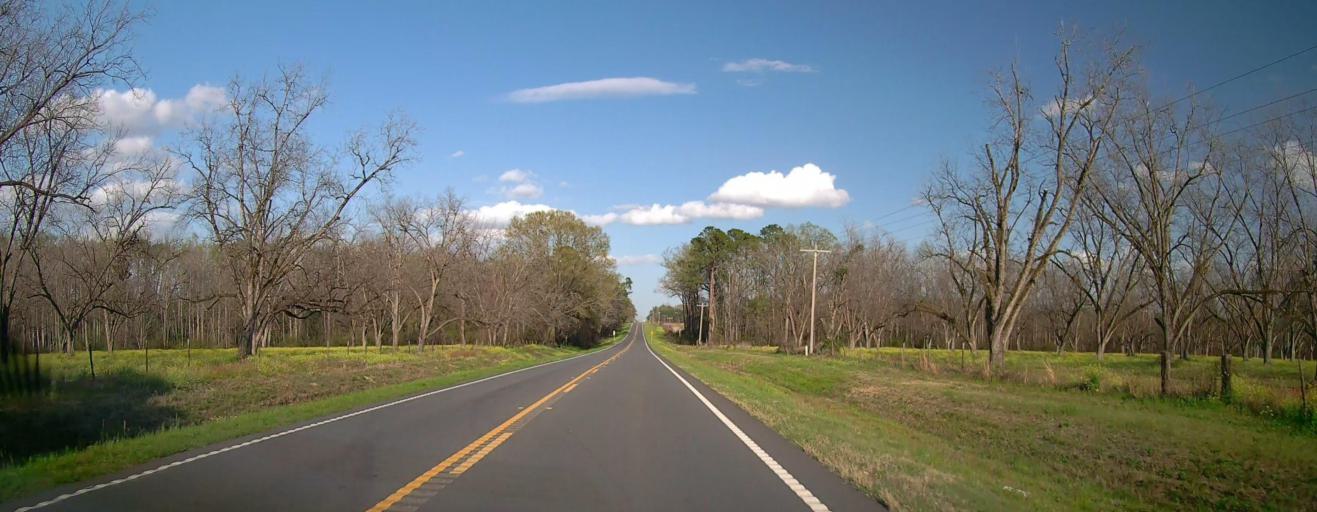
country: US
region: Georgia
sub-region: Toombs County
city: Vidalia
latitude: 32.1985
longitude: -82.4999
